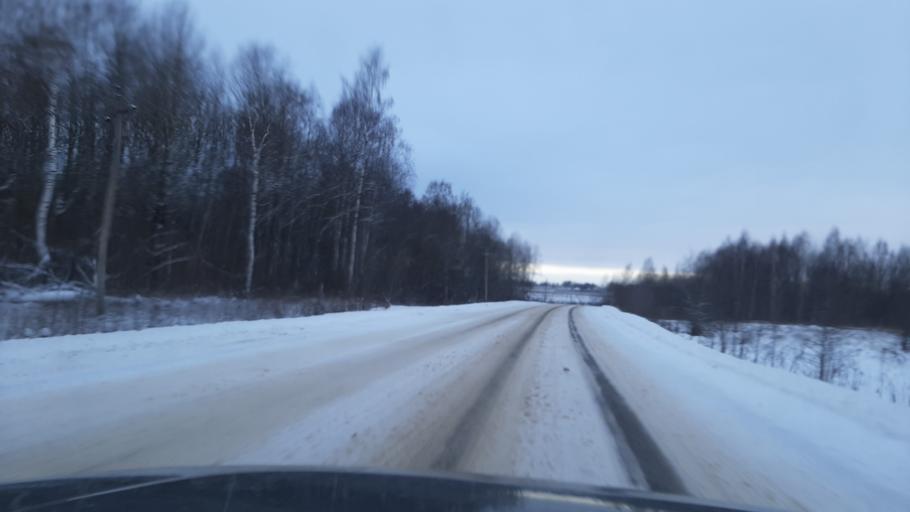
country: RU
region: Kostroma
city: Volgorechensk
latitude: 57.4429
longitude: 41.0349
